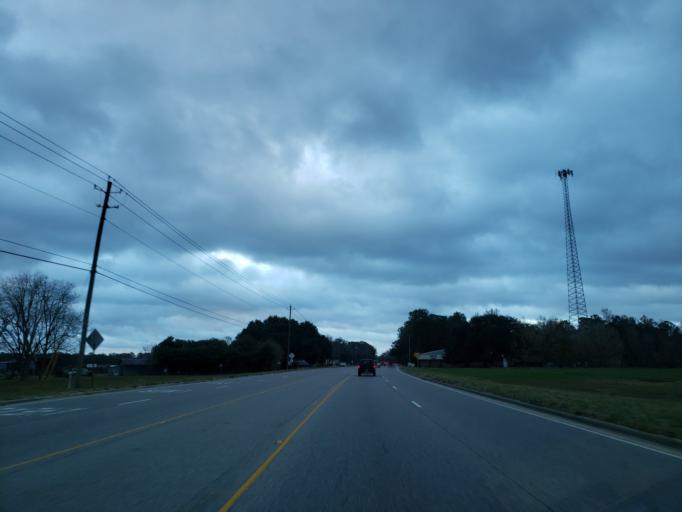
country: US
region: Alabama
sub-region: Mobile County
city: Prichard
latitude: 30.7834
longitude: -88.2741
